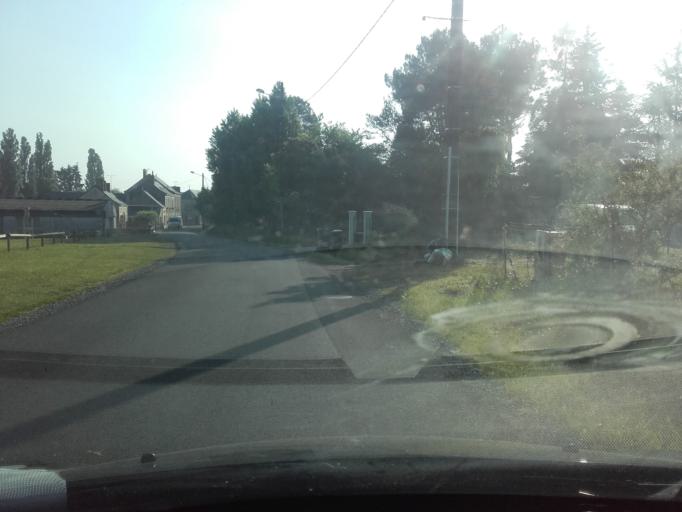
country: FR
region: Centre
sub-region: Departement d'Indre-et-Loire
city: Mazieres-de-Touraine
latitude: 47.3824
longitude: 0.4212
